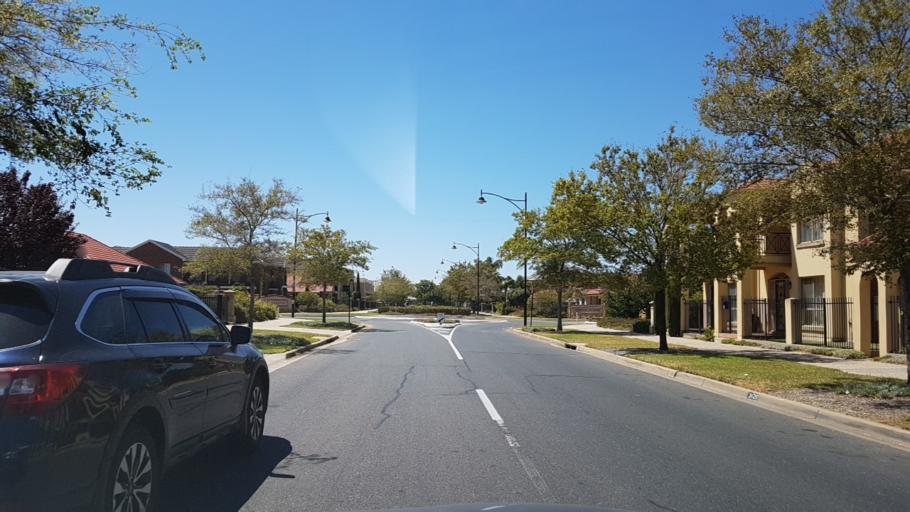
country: AU
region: South Australia
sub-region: Salisbury
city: Ingle Farm
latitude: -34.8129
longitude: 138.6080
